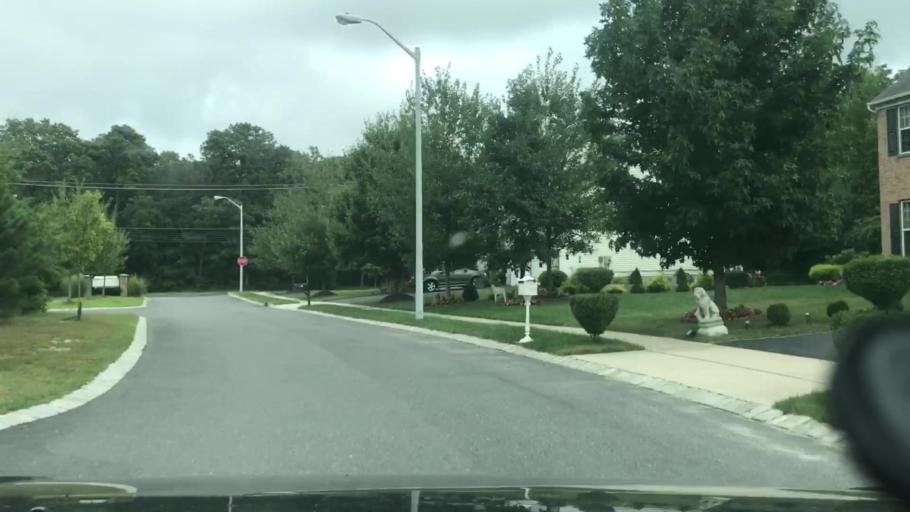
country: US
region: New Jersey
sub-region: Ocean County
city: Barnegat
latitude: 39.7521
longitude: -74.2413
